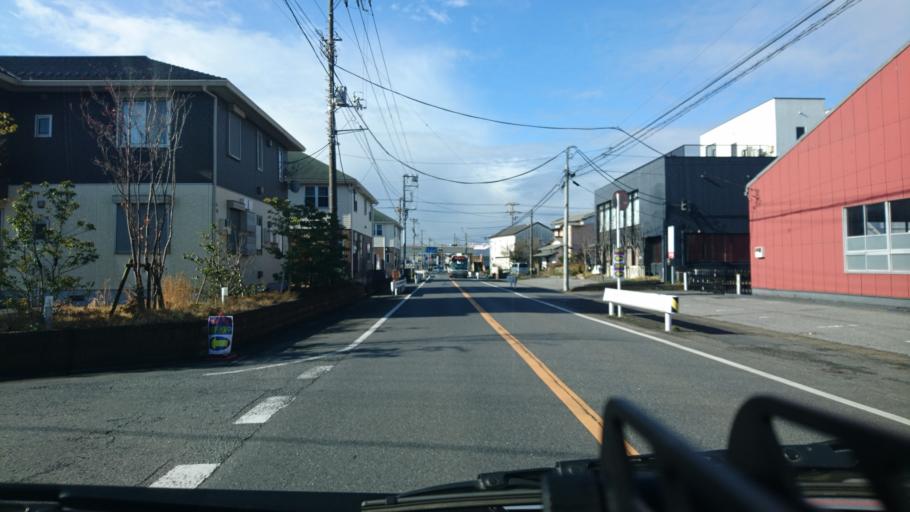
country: JP
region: Chiba
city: Kisarazu
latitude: 35.3699
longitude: 139.9229
